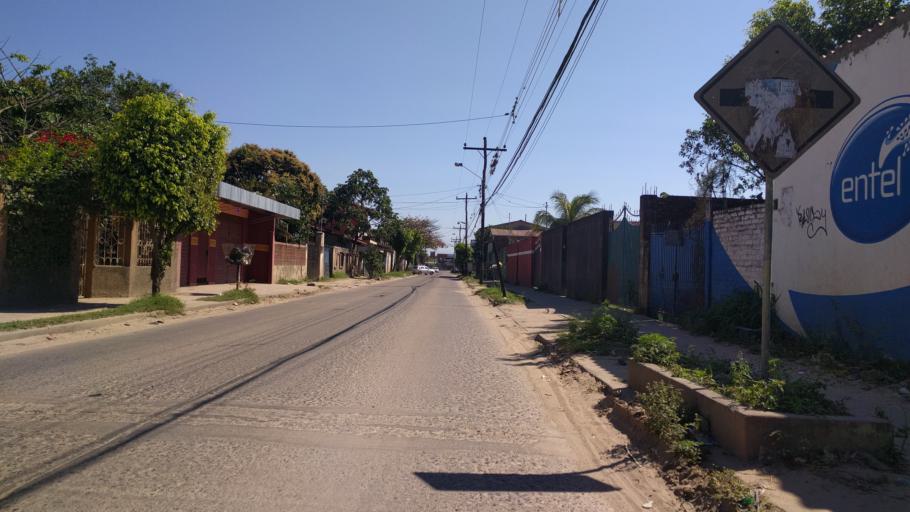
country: BO
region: Santa Cruz
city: Santa Cruz de la Sierra
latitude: -17.8309
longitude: -63.2265
